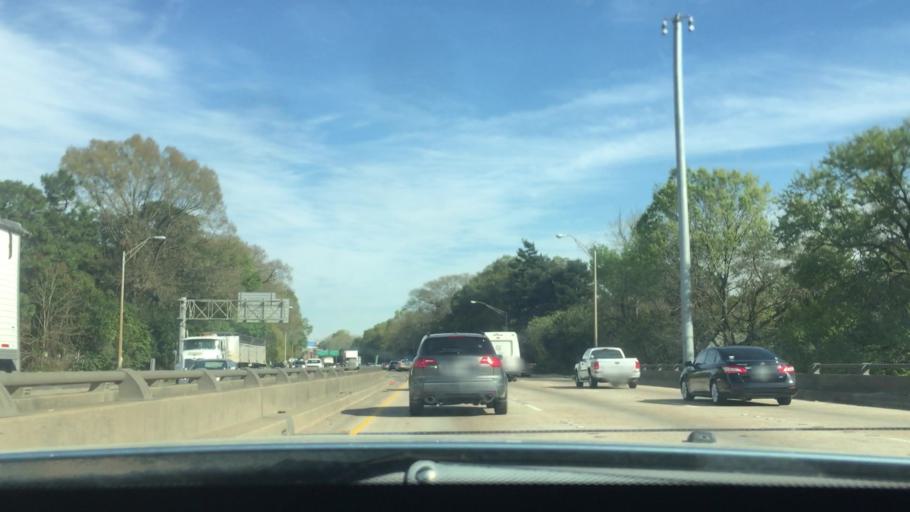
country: US
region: Louisiana
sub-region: East Baton Rouge Parish
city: Baton Rouge
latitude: 30.4263
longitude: -91.1667
